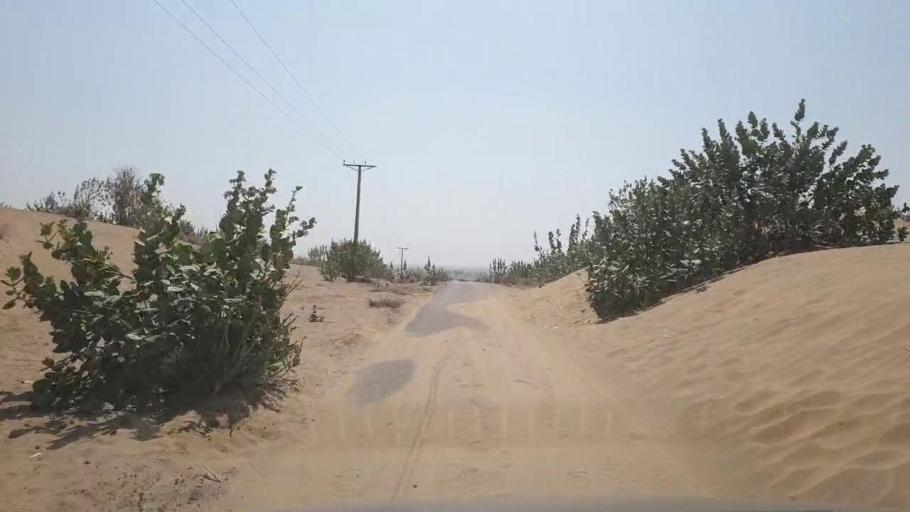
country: PK
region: Sindh
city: Chor
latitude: 25.6164
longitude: 70.1766
